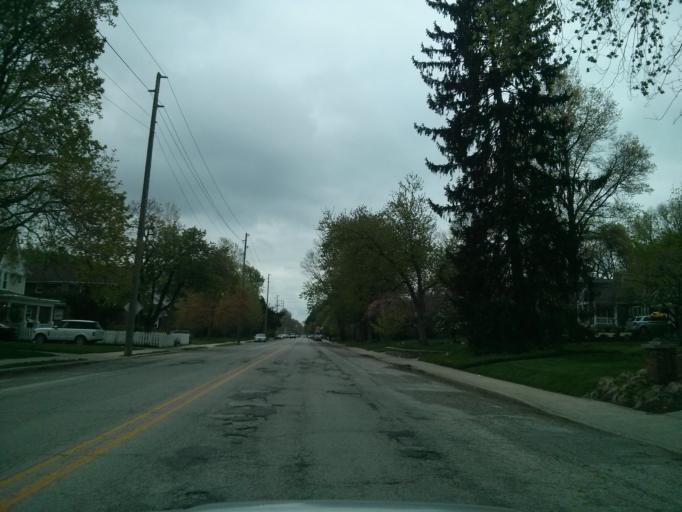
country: US
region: Indiana
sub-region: Marion County
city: Broad Ripple
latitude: 39.8461
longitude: -86.1543
